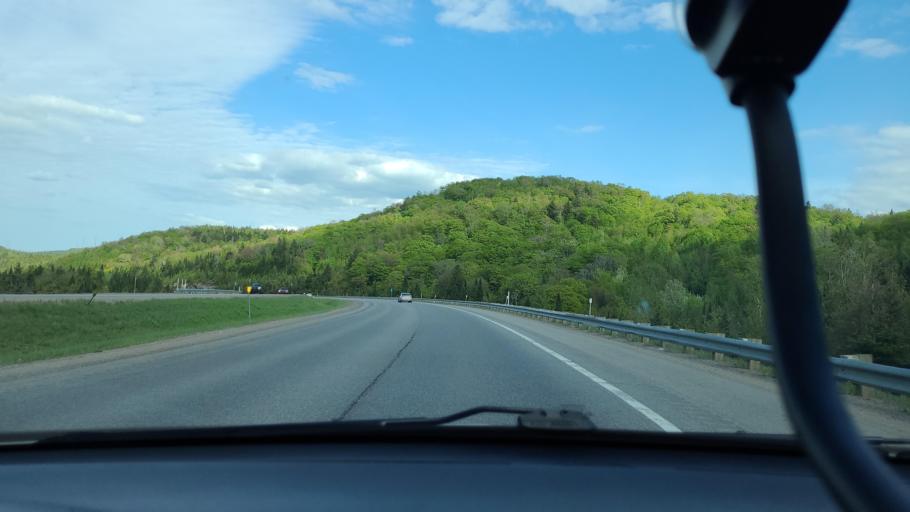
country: CA
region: Quebec
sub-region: Laurentides
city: Val-David
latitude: 45.9889
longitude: -74.2156
